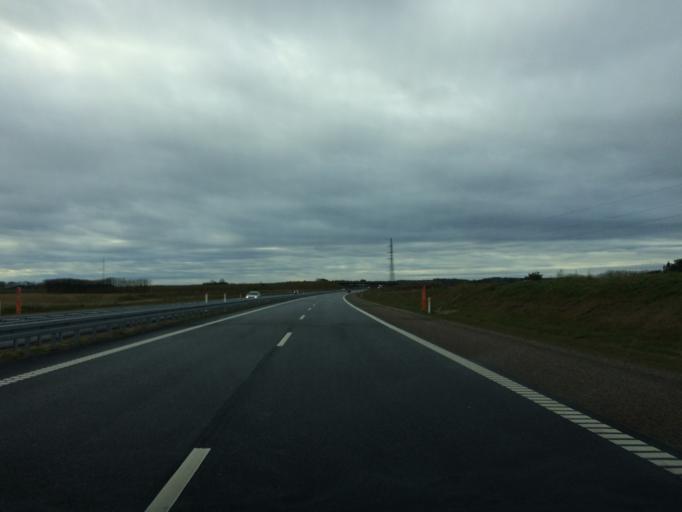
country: DK
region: Central Jutland
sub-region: Silkeborg Kommune
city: Silkeborg
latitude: 56.1514
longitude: 9.4524
